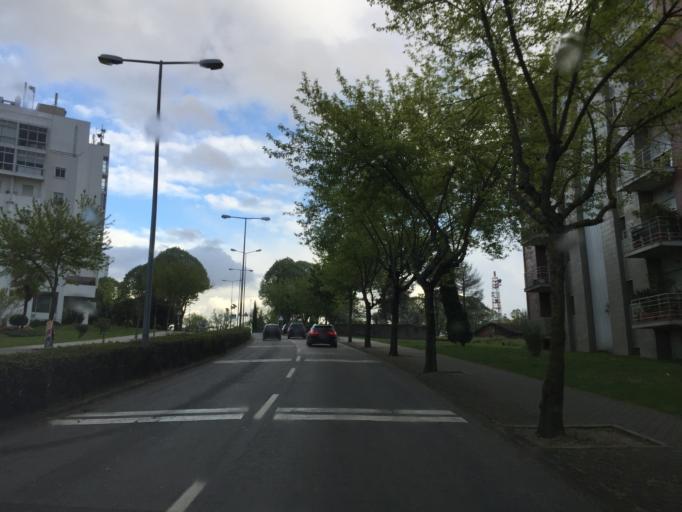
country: PT
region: Viseu
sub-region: Viseu
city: Viseu
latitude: 40.6508
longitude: -7.9209
